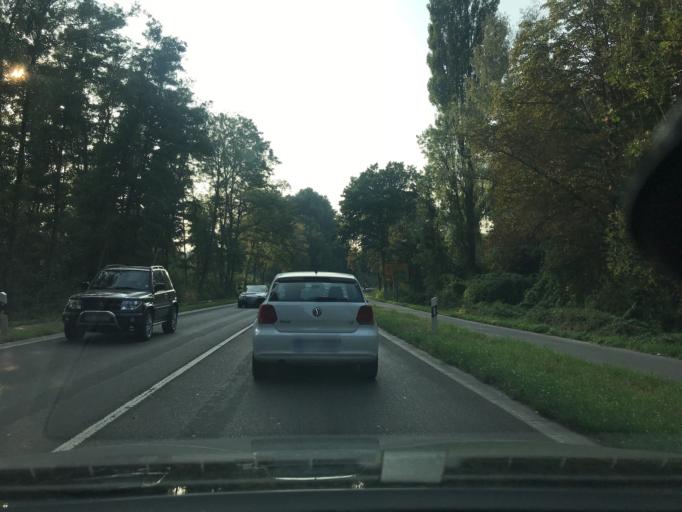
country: DE
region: North Rhine-Westphalia
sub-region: Regierungsbezirk Dusseldorf
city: Erkrath
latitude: 51.1995
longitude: 6.8902
